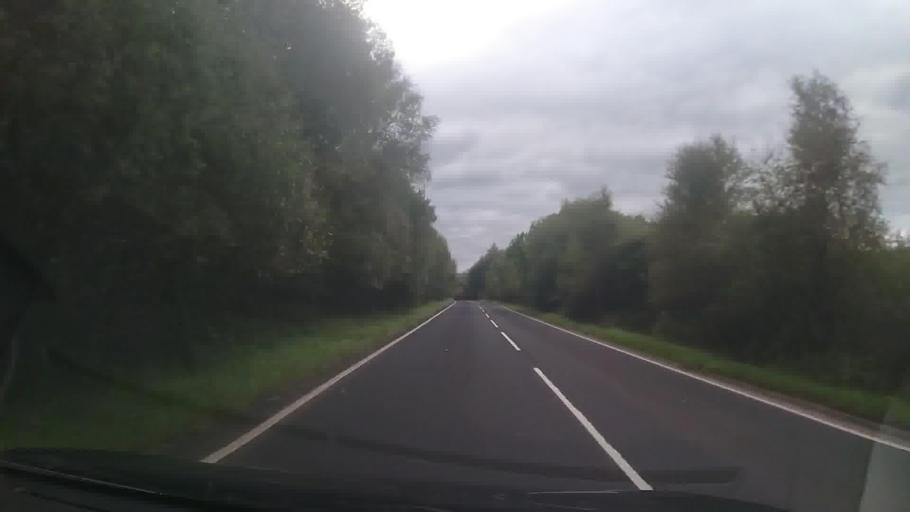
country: GB
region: Scotland
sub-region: Argyll and Bute
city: Garelochhead
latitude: 56.2291
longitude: -5.0035
